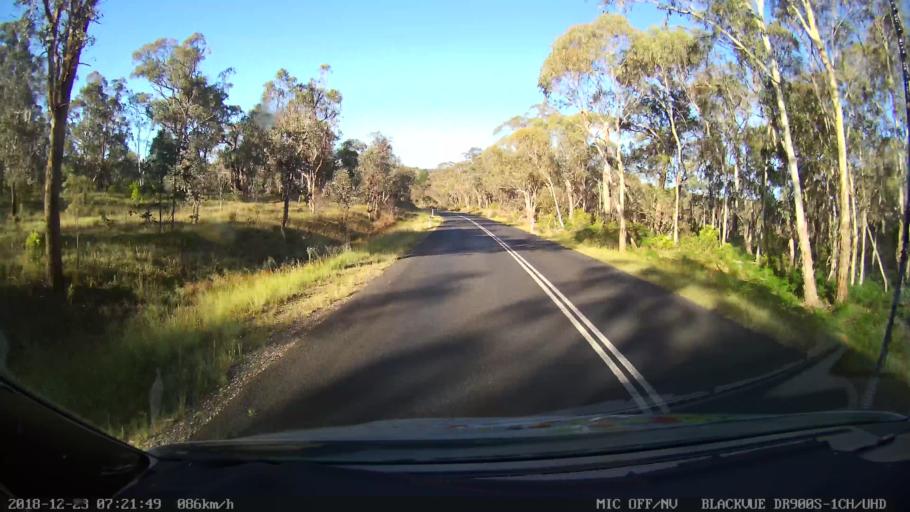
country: AU
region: New South Wales
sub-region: Bellingen
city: Dorrigo
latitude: -30.4974
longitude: 152.2575
